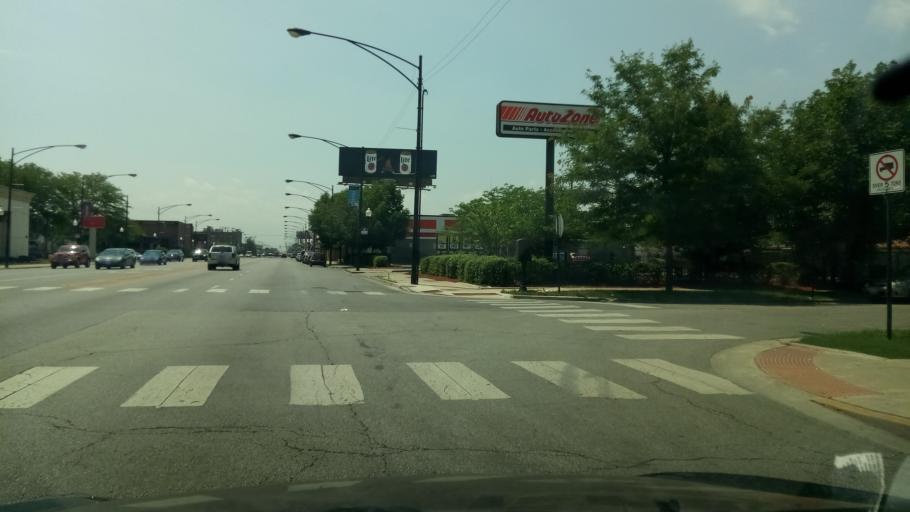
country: US
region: Illinois
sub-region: Cook County
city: Hometown
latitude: 41.7830
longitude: -87.7229
